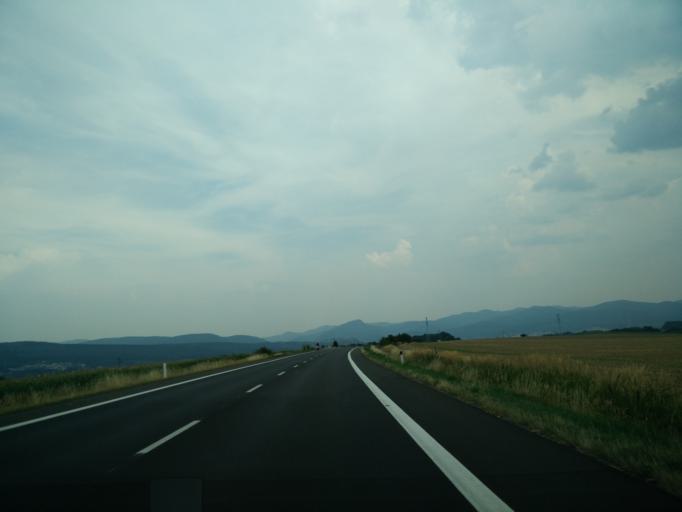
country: SK
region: Banskobystricky
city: Ziar nad Hronom
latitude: 48.6189
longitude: 18.8092
